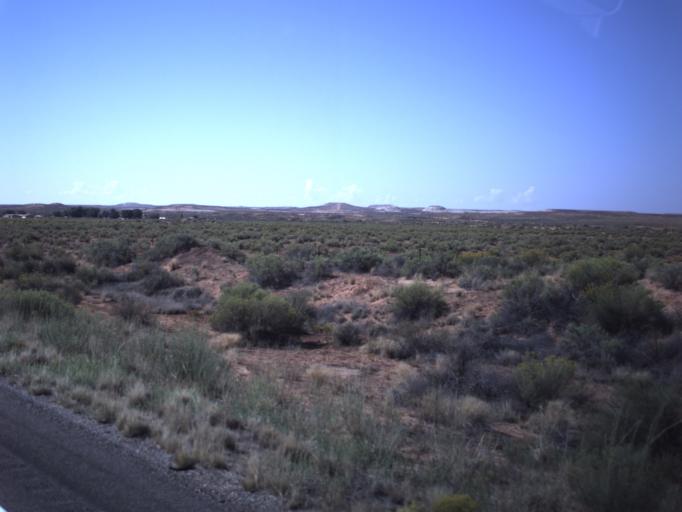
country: US
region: Utah
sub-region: San Juan County
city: Blanding
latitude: 37.1139
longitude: -109.5456
